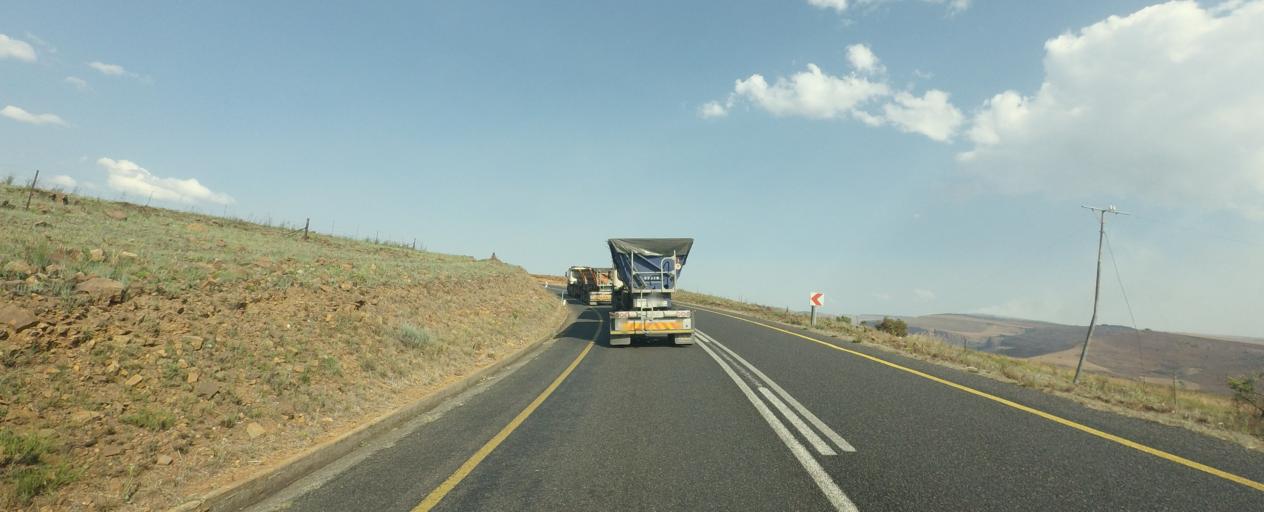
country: ZA
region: Mpumalanga
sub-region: Ehlanzeni District
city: Lydenburg
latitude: -25.1131
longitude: 30.5040
